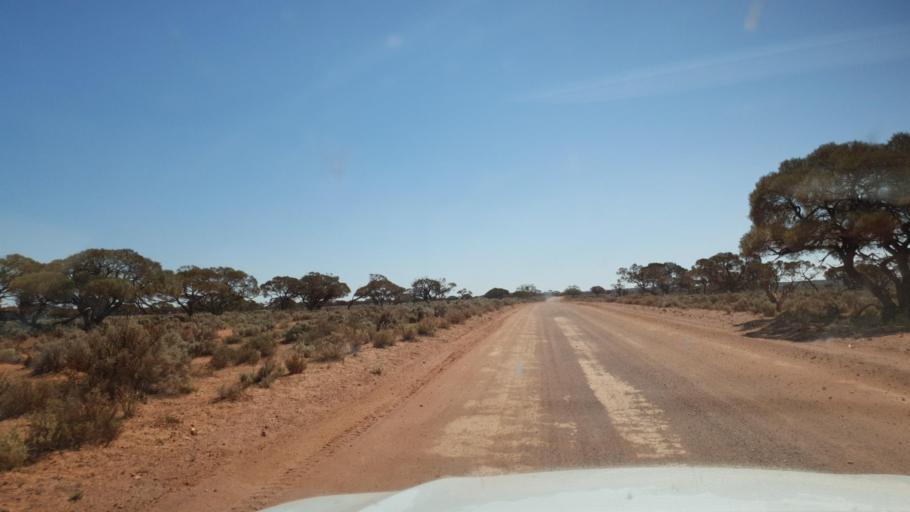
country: AU
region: South Australia
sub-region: Whyalla
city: Whyalla
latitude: -32.6676
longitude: 137.0621
